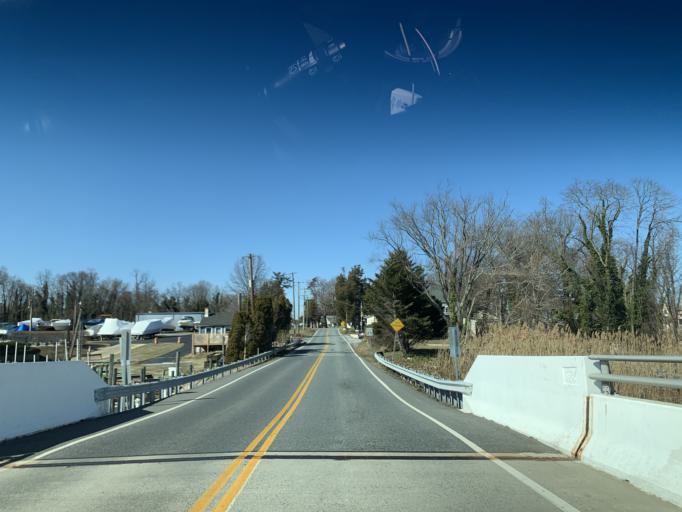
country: US
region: Maryland
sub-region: Cecil County
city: Charlestown
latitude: 39.4619
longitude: -75.8761
